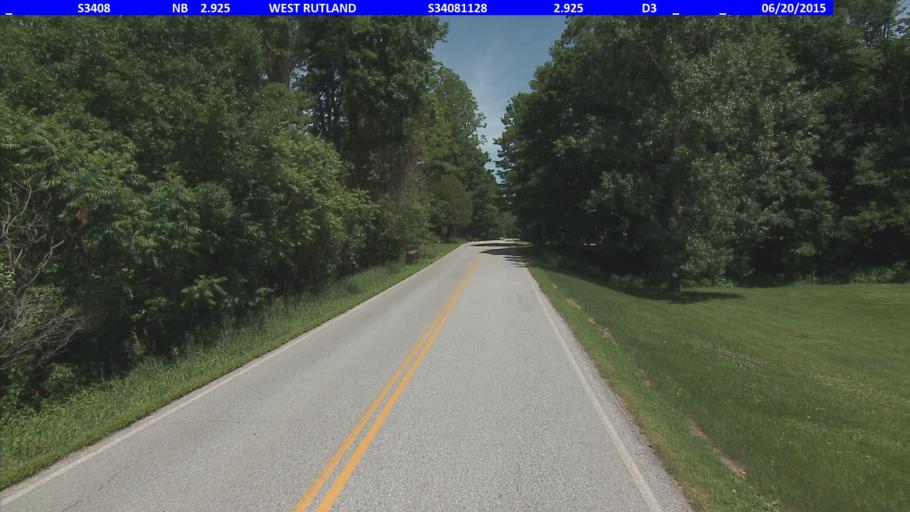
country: US
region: Vermont
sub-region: Rutland County
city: West Rutland
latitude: 43.6510
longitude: -73.0732
